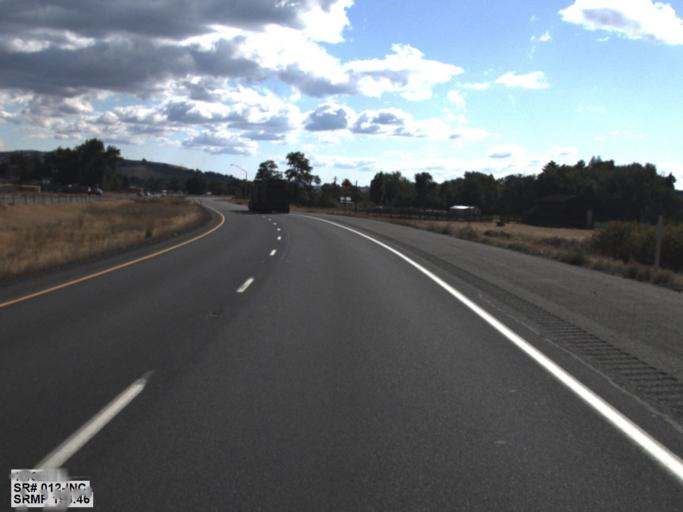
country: US
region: Washington
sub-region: Yakima County
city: Gleed
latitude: 46.6564
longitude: -120.6176
